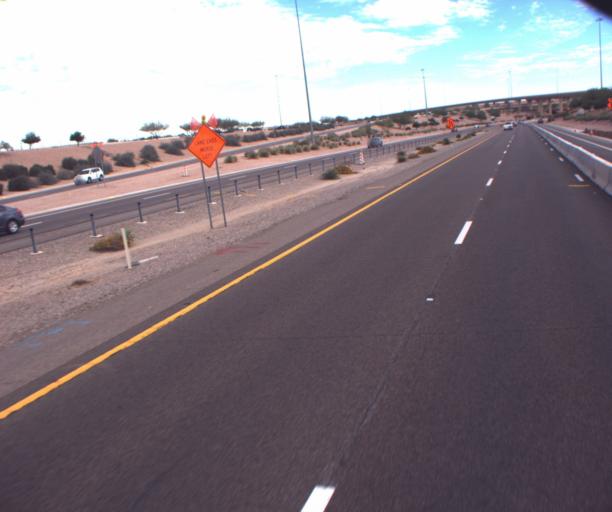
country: US
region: Arizona
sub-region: Maricopa County
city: Guadalupe
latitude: 33.2945
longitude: -111.9803
